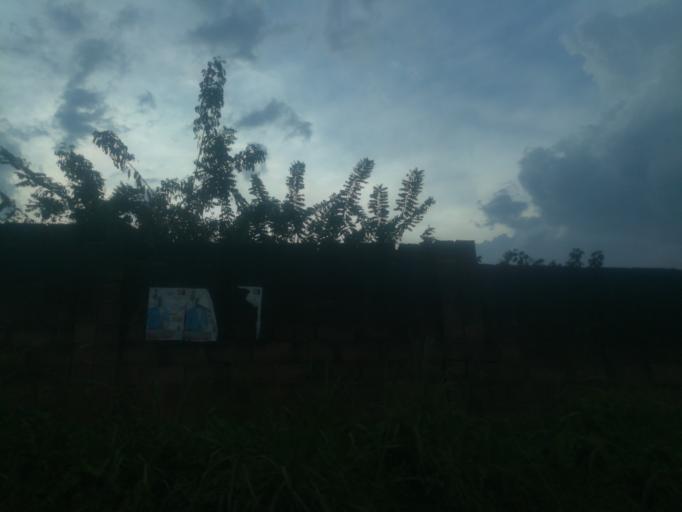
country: NG
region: Oyo
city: Ibadan
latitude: 7.3857
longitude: 3.8362
